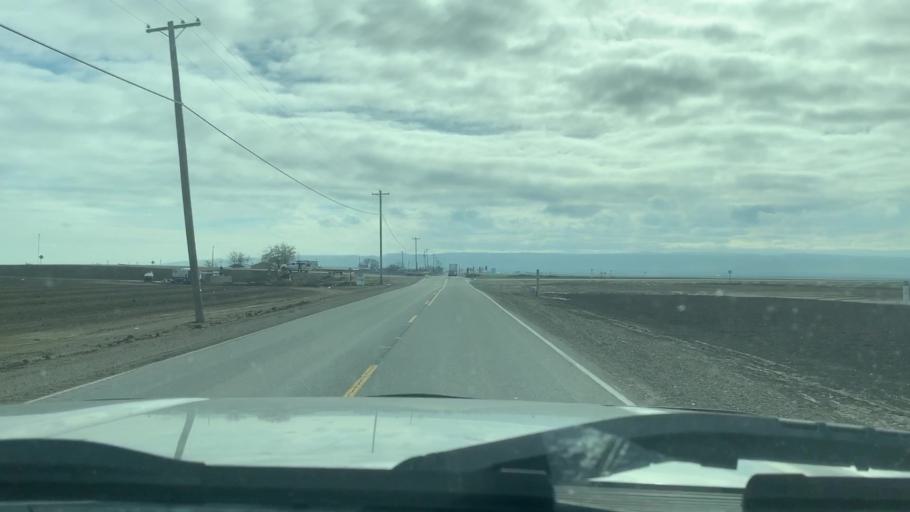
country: US
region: California
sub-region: Merced County
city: Los Banos
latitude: 36.9795
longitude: -120.8374
